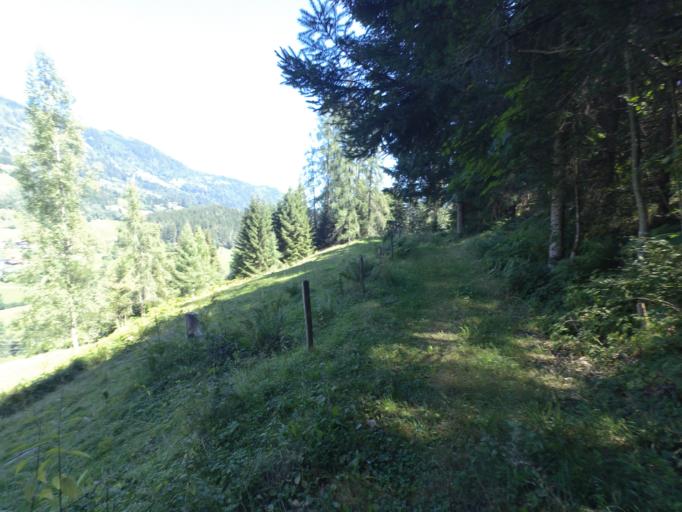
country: AT
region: Salzburg
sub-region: Politischer Bezirk Sankt Johann im Pongau
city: Goldegg
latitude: 47.3286
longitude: 13.1222
